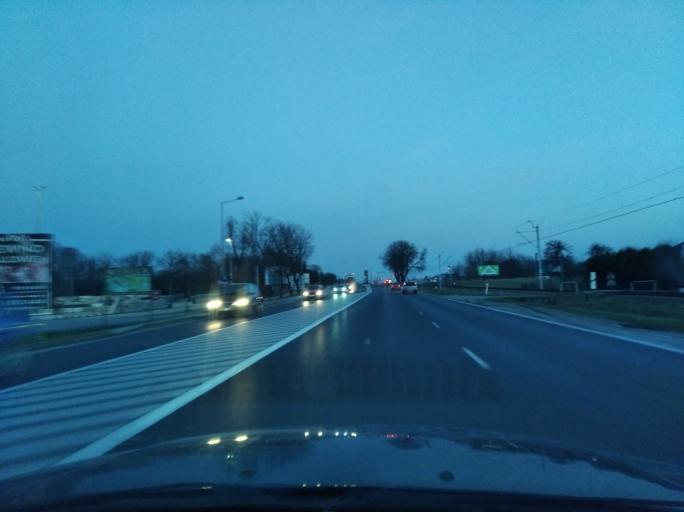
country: PL
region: Subcarpathian Voivodeship
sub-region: Rzeszow
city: Rzeszow
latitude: 50.0746
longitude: 21.9879
